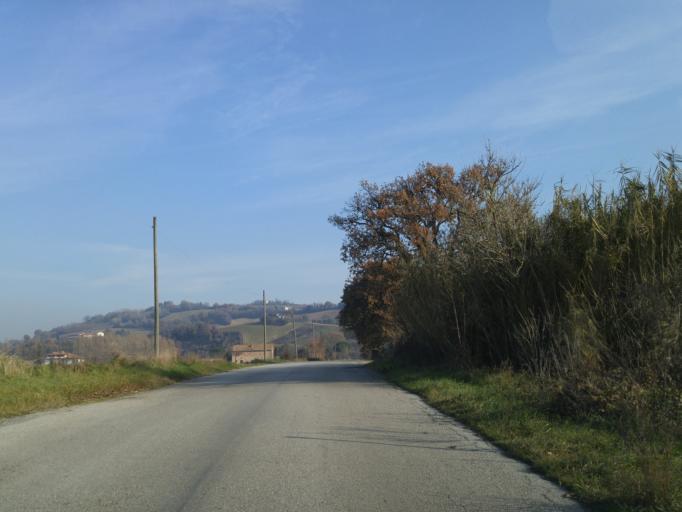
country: IT
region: The Marches
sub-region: Provincia di Pesaro e Urbino
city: Tavernelle
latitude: 43.7116
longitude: 12.8919
